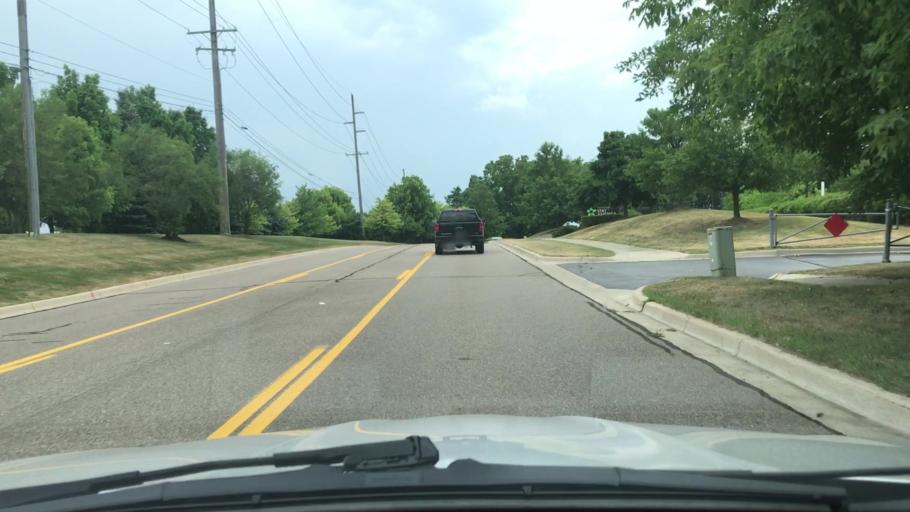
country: US
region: Michigan
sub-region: Wayne County
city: Northville
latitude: 42.4416
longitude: -83.4386
